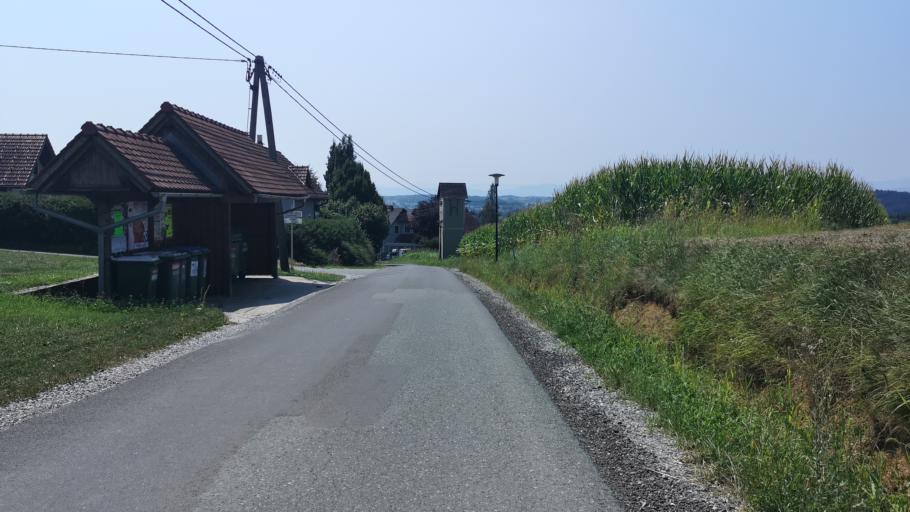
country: AT
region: Styria
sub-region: Politischer Bezirk Deutschlandsberg
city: Preding
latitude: 46.8655
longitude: 15.3893
